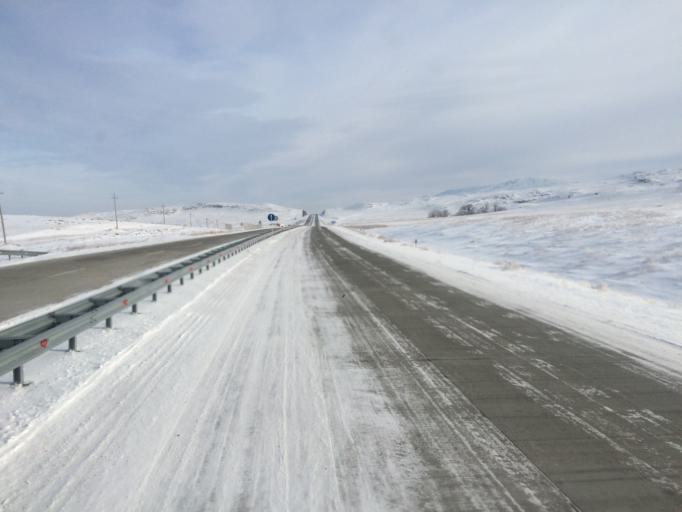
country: KZ
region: Zhambyl
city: Georgiyevka
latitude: 43.4341
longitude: 74.9282
